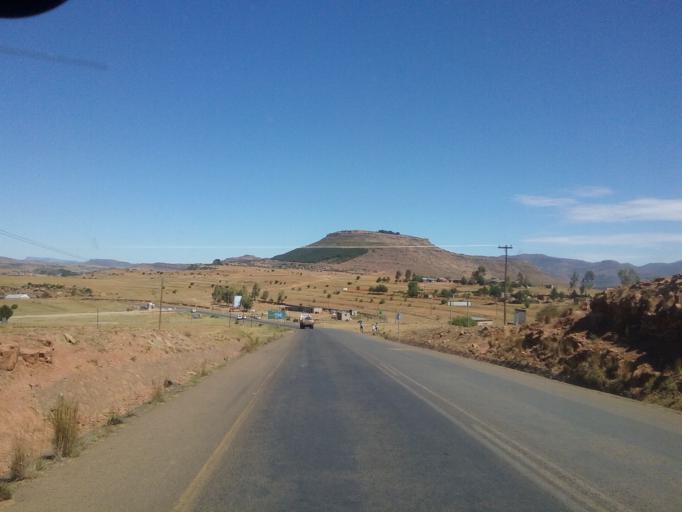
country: LS
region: Quthing
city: Quthing
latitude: -30.3903
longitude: 27.6262
